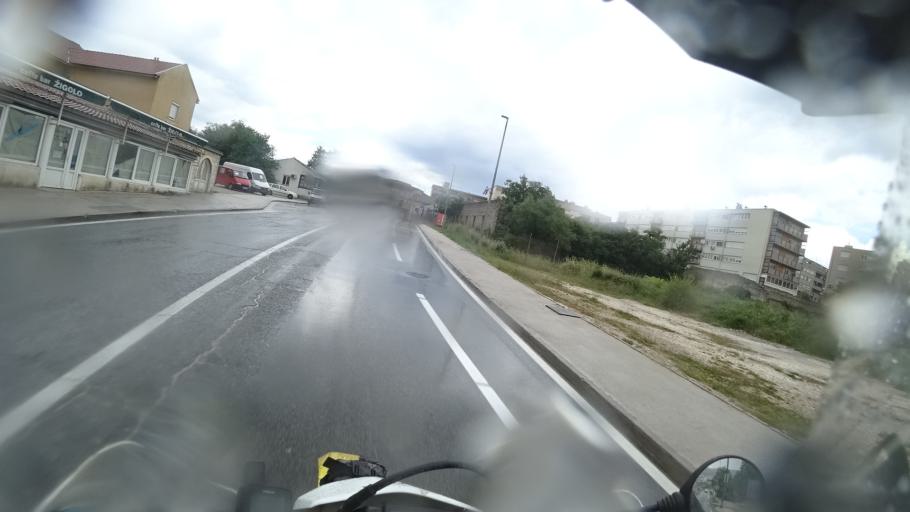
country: HR
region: Sibensko-Kniniska
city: Knin
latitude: 44.0419
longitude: 16.1986
